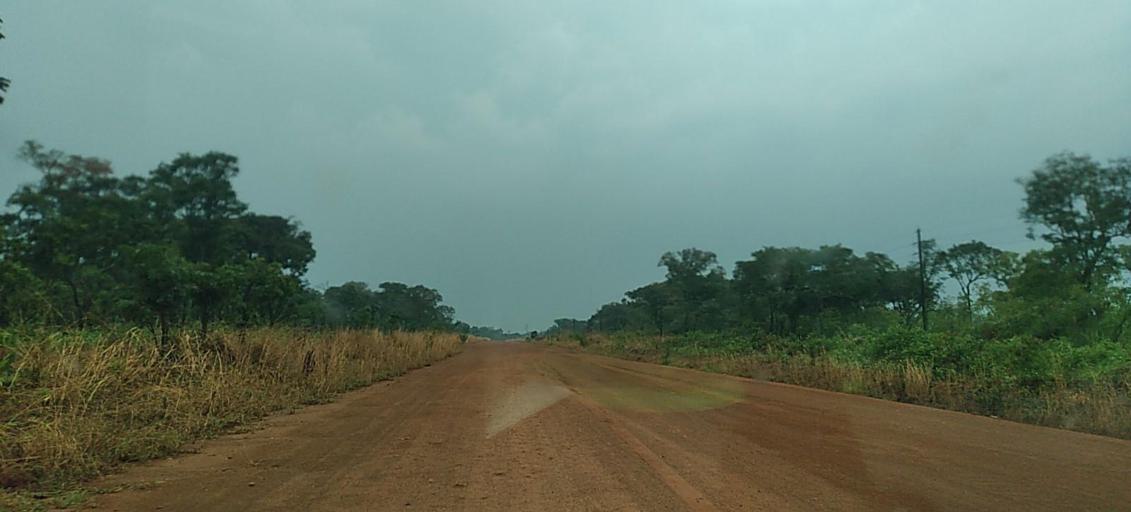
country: ZM
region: North-Western
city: Mwinilunga
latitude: -11.6102
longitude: 24.3978
